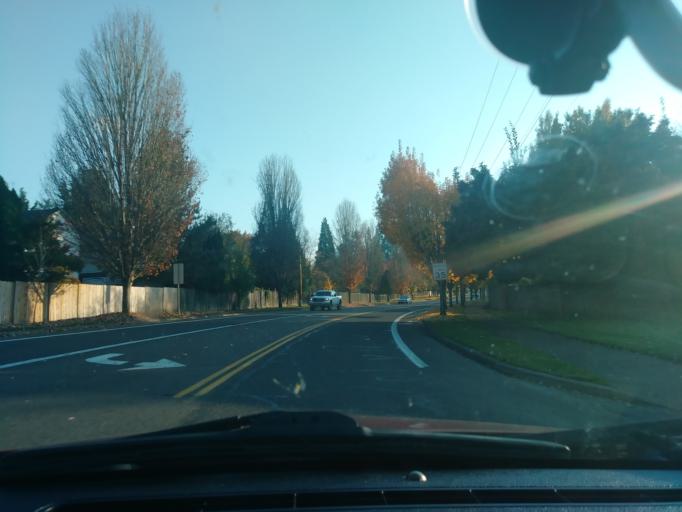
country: US
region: Oregon
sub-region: Washington County
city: Forest Grove
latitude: 45.5270
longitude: -123.1211
